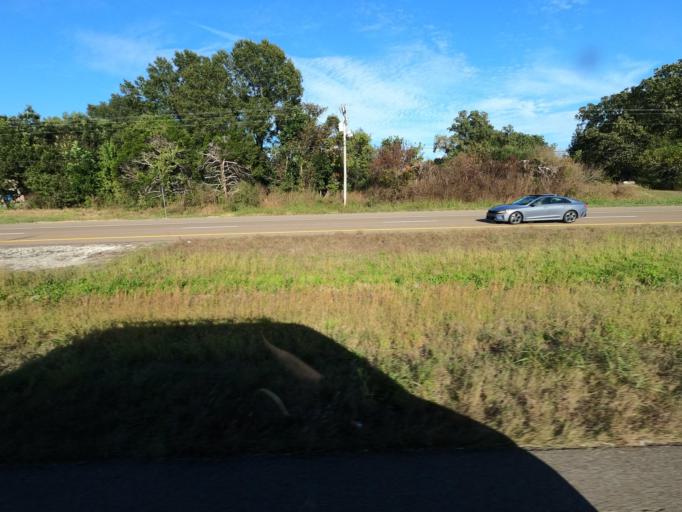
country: US
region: Tennessee
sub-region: Crockett County
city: Bells
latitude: 35.7155
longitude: -89.0552
